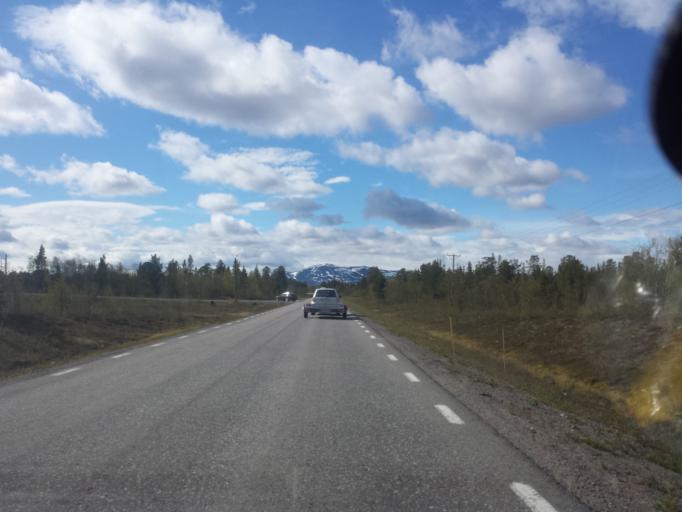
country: SE
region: Norrbotten
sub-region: Kiruna Kommun
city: Kiruna
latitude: 67.9923
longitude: 19.9152
